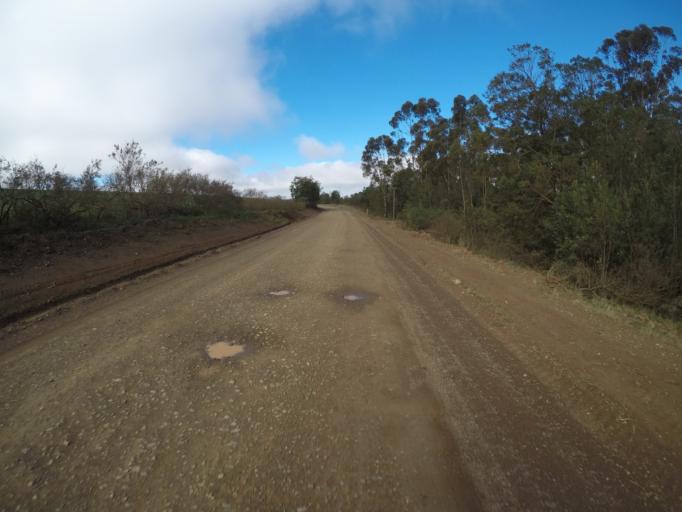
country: ZA
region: Western Cape
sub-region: Overberg District Municipality
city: Caledon
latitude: -34.1127
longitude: 19.7716
